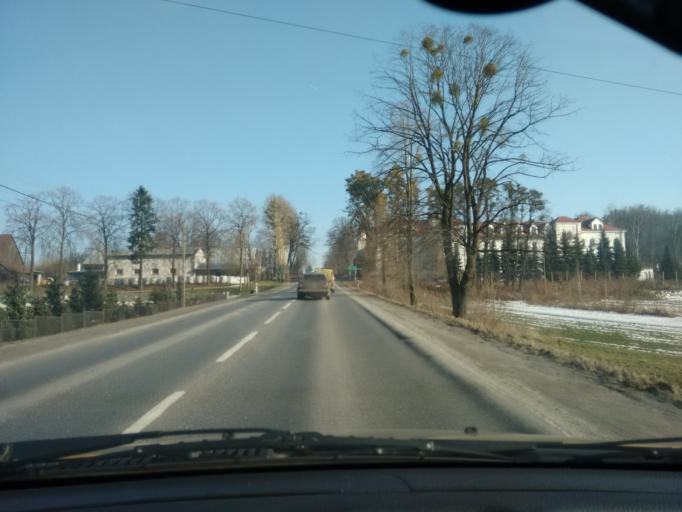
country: PL
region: Lesser Poland Voivodeship
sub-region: Powiat wadowicki
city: Jaroszowice
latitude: 49.8745
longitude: 19.5243
